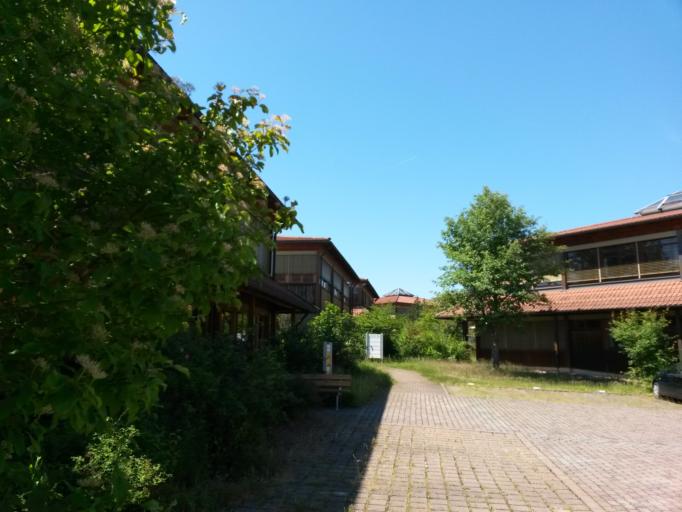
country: DE
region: Bavaria
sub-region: Regierungsbezirk Unterfranken
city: Rimpar
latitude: 49.8487
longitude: 9.9667
